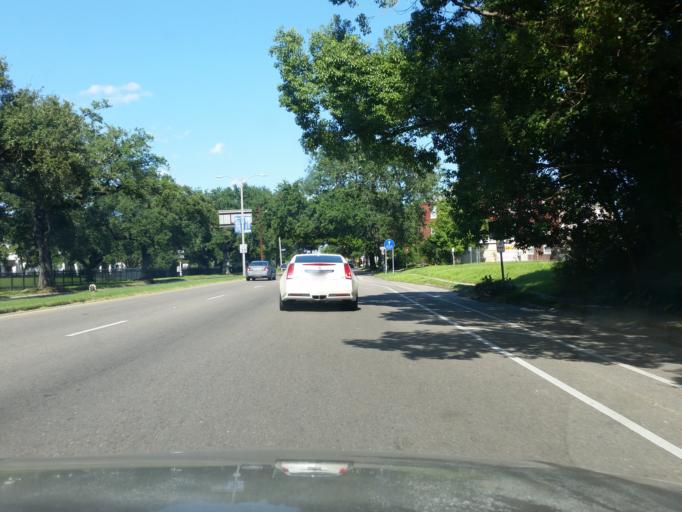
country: US
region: Louisiana
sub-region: Orleans Parish
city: New Orleans
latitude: 29.9937
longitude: -90.0656
